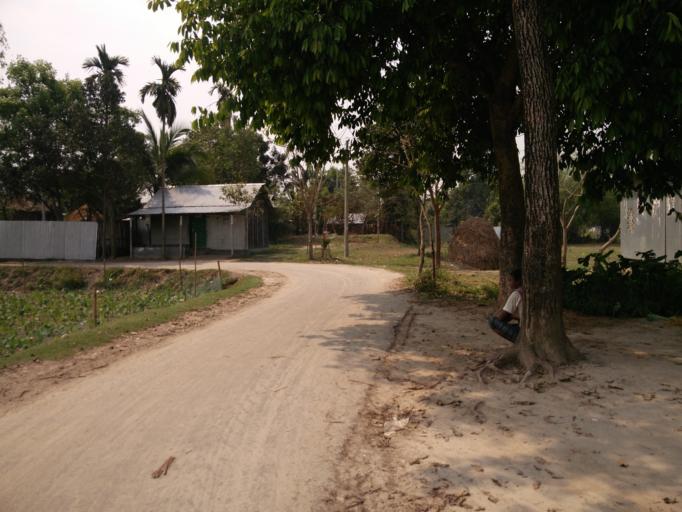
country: BD
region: Dhaka
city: Muktagacha
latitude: 24.8879
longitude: 90.2735
